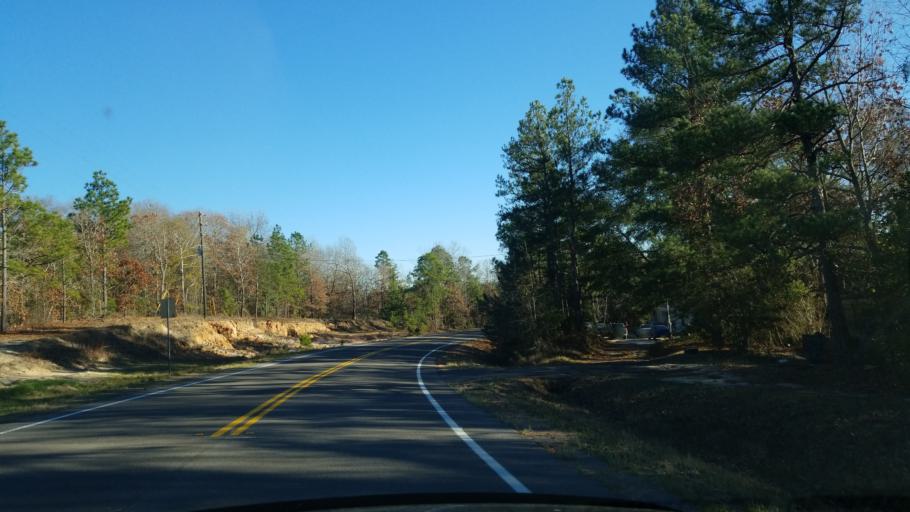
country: US
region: Georgia
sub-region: Talbot County
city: Talbotton
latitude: 32.5757
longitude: -84.5424
